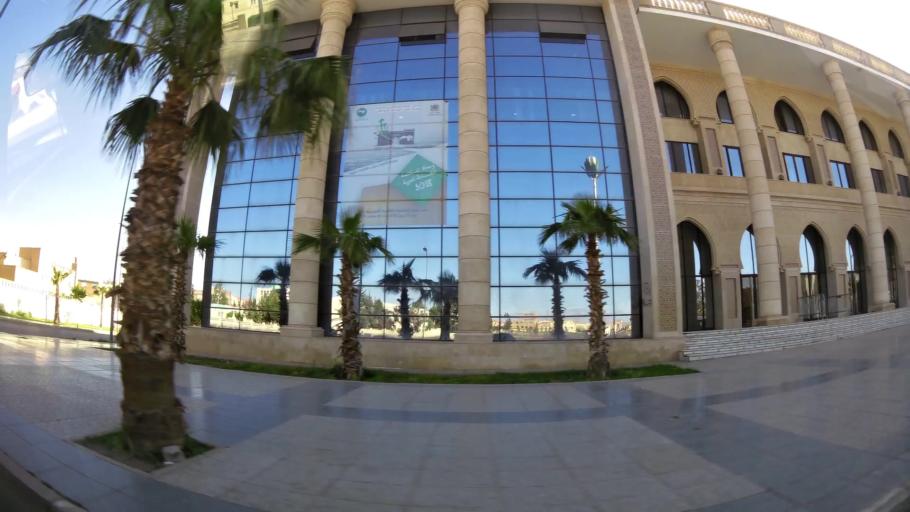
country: MA
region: Oriental
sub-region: Oujda-Angad
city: Oujda
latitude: 34.6788
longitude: -1.9309
